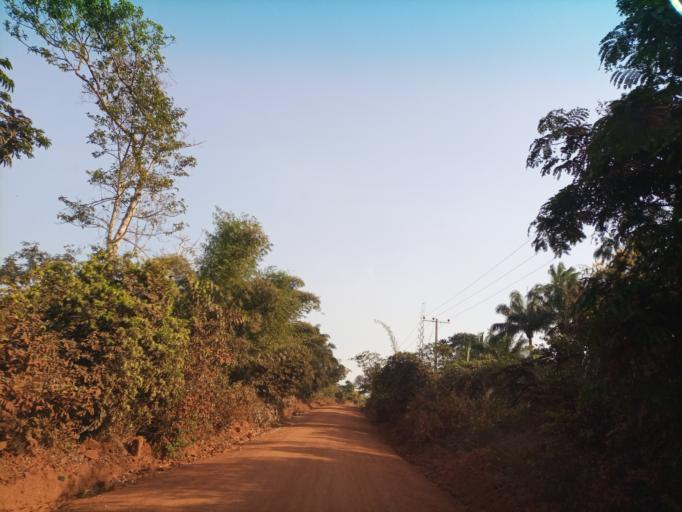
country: NG
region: Enugu
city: Opi
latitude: 6.7655
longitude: 7.3954
